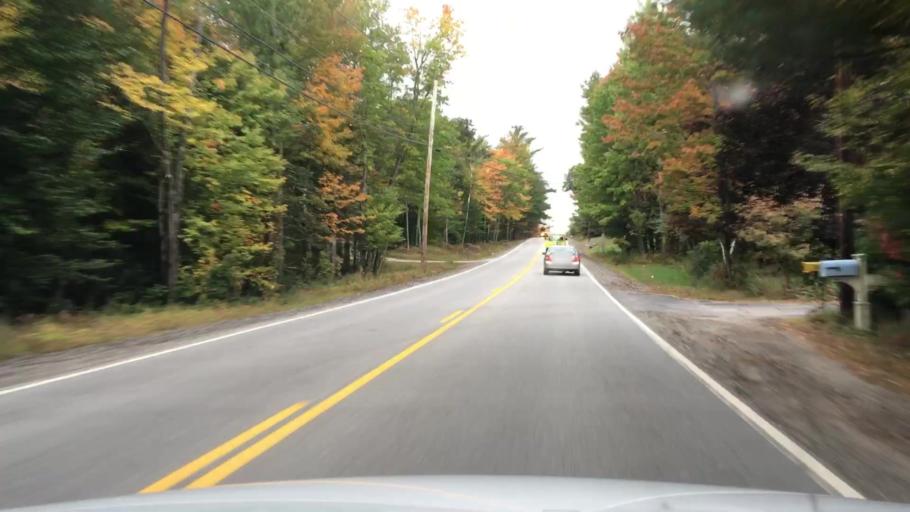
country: US
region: Maine
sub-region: Oxford County
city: Norway
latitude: 44.2224
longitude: -70.6380
